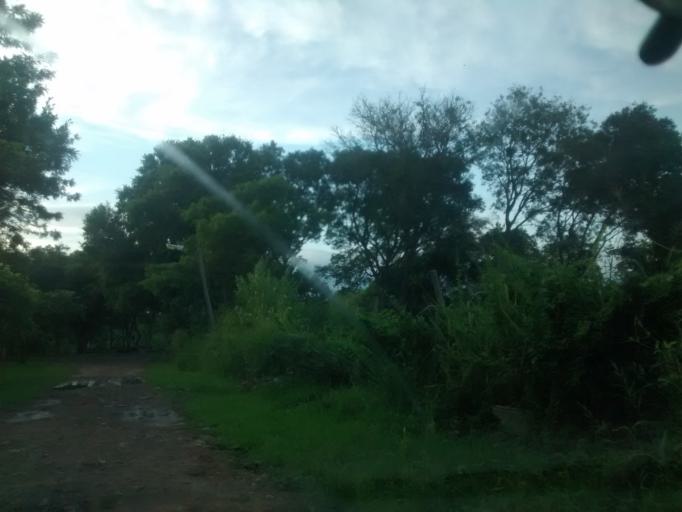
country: AR
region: Chaco
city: Fontana
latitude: -27.4201
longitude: -59.0030
